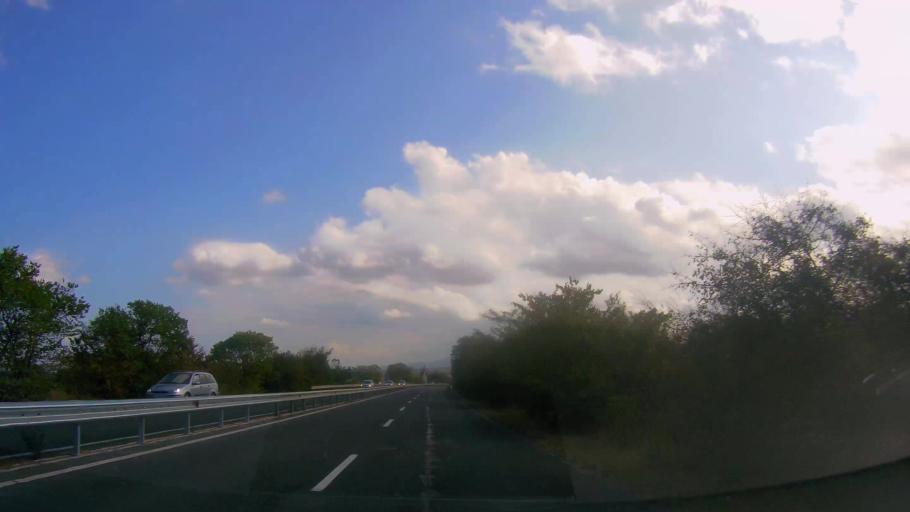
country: BG
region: Burgas
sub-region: Obshtina Sozopol
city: Chernomorets
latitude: 42.4314
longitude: 27.6388
